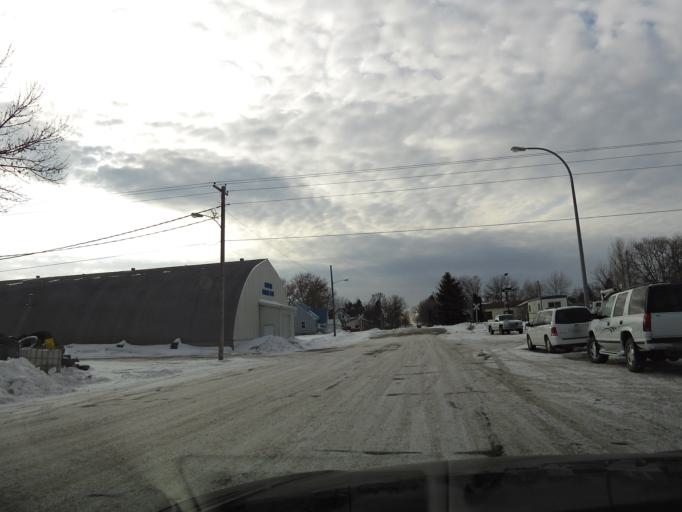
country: US
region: North Dakota
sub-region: Walsh County
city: Grafton
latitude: 48.5630
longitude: -97.1780
